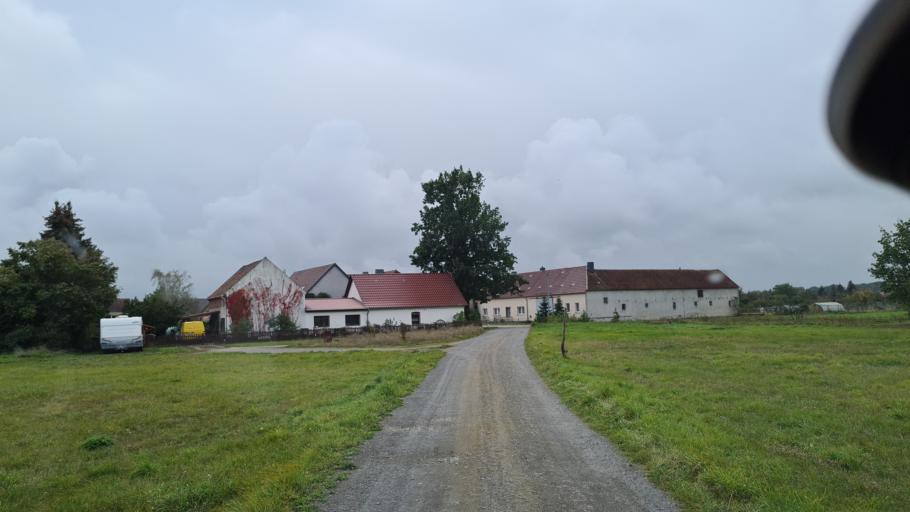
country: DE
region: Brandenburg
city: Schonewalde
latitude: 51.7014
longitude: 13.5732
